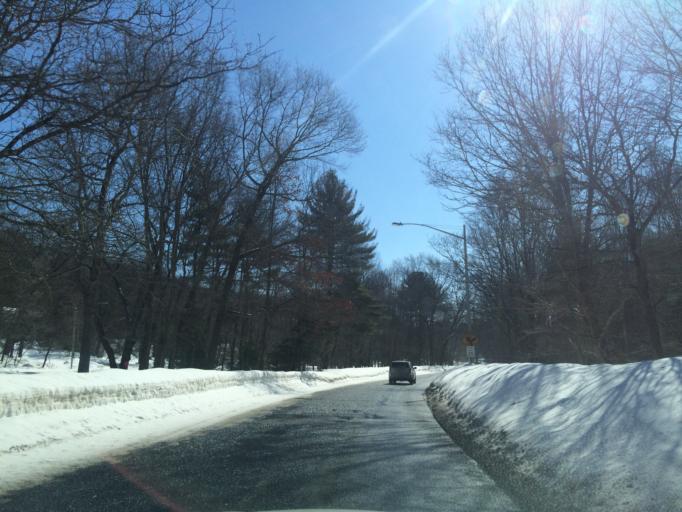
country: US
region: Massachusetts
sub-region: Norfolk County
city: Wellesley
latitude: 42.2969
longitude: -71.2762
